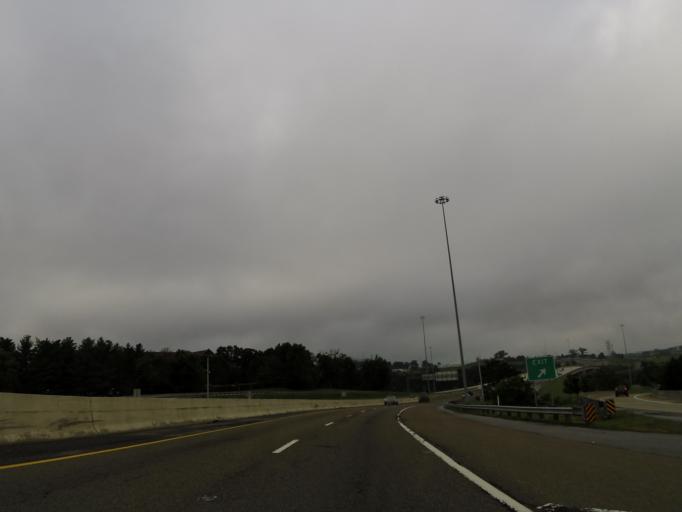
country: US
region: Tennessee
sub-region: Knox County
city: Knoxville
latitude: 35.9512
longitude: -83.9426
